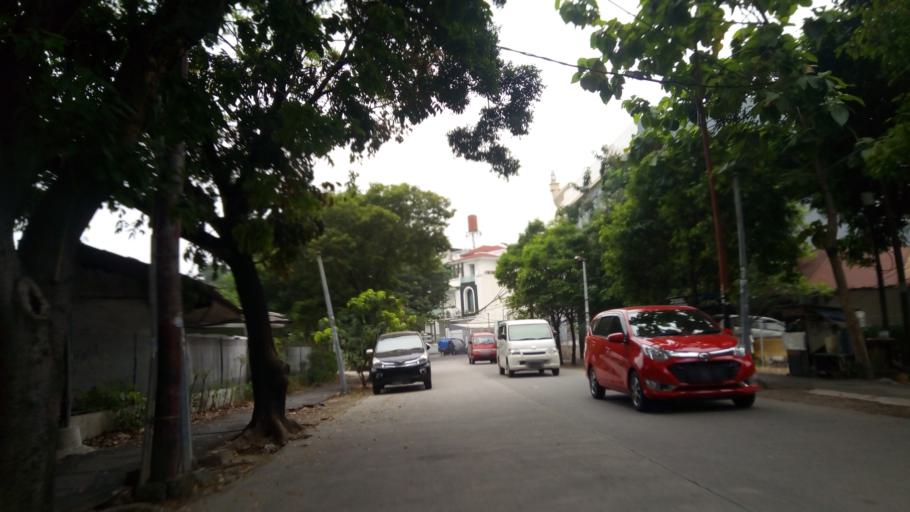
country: ID
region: Jakarta Raya
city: Jakarta
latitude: -6.1492
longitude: 106.8416
